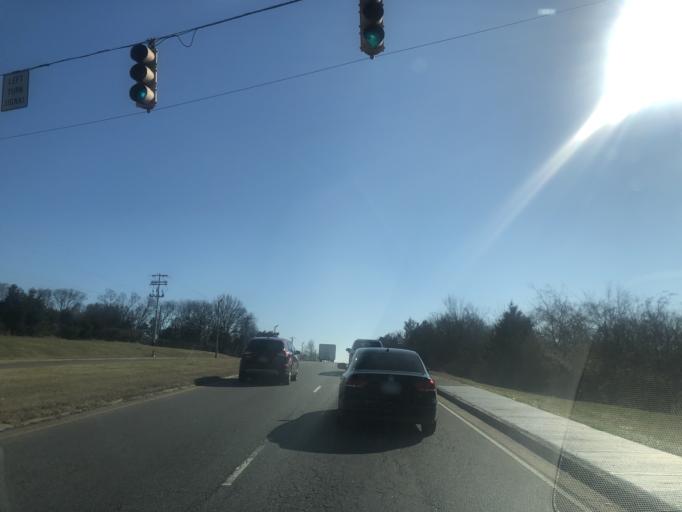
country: US
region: Tennessee
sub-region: Rutherford County
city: Smyrna
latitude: 35.9530
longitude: -86.5136
